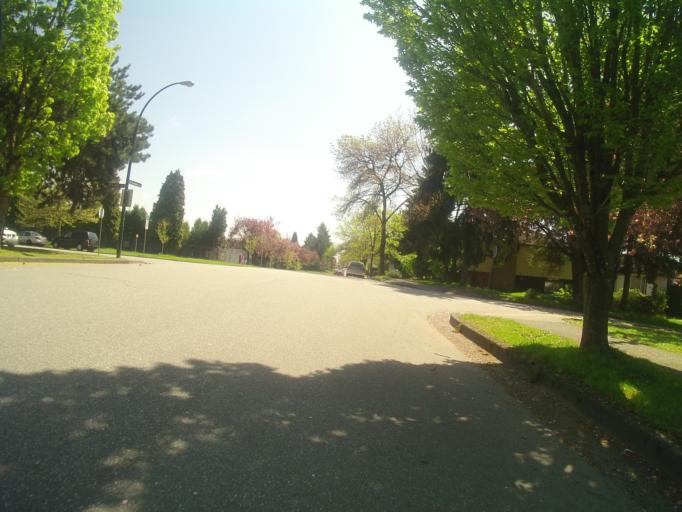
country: CA
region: British Columbia
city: Vancouver
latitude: 49.2279
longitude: -123.0800
